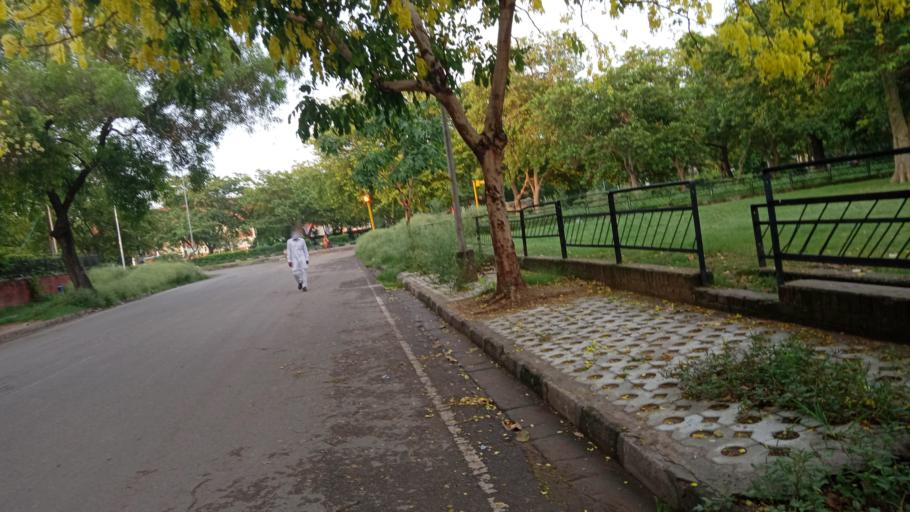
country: IN
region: Chandigarh
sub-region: Chandigarh
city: Chandigarh
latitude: 30.7478
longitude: 76.7507
